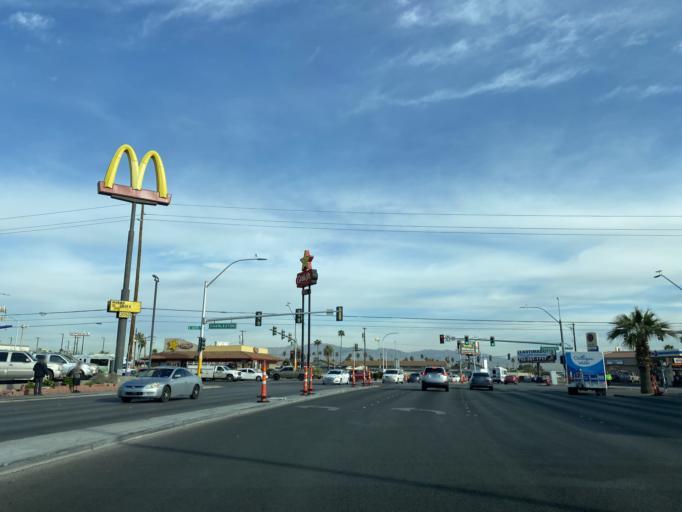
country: US
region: Nevada
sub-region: Clark County
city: Las Vegas
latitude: 36.1582
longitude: -115.1188
